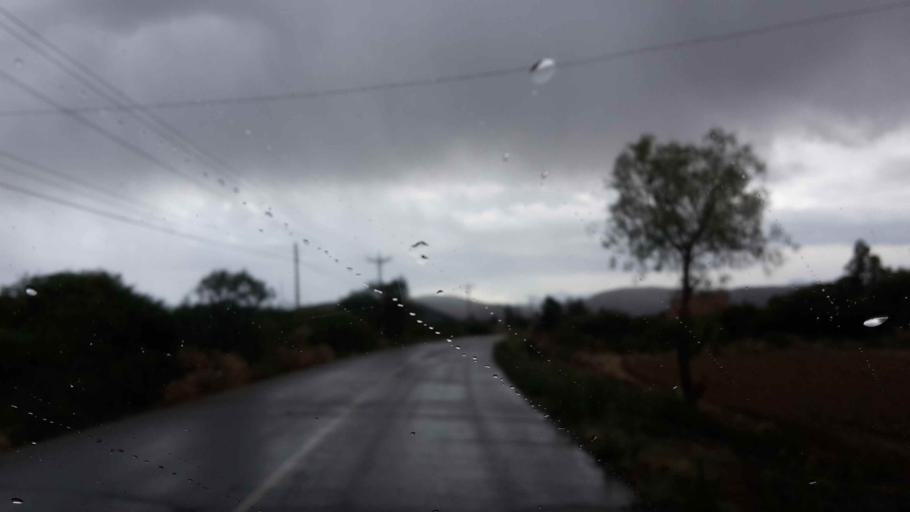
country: BO
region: Cochabamba
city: Tarata
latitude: -17.5676
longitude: -66.0760
